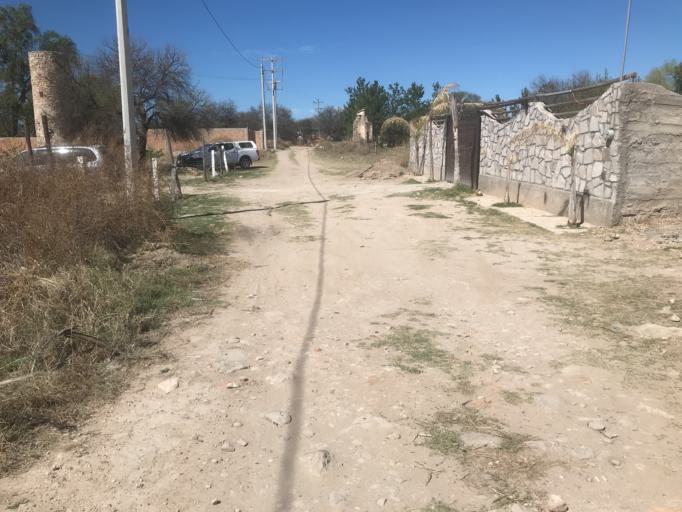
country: MX
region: Durango
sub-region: Durango
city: Sebastian Lerdo de Tejada
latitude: 23.9746
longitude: -104.6161
